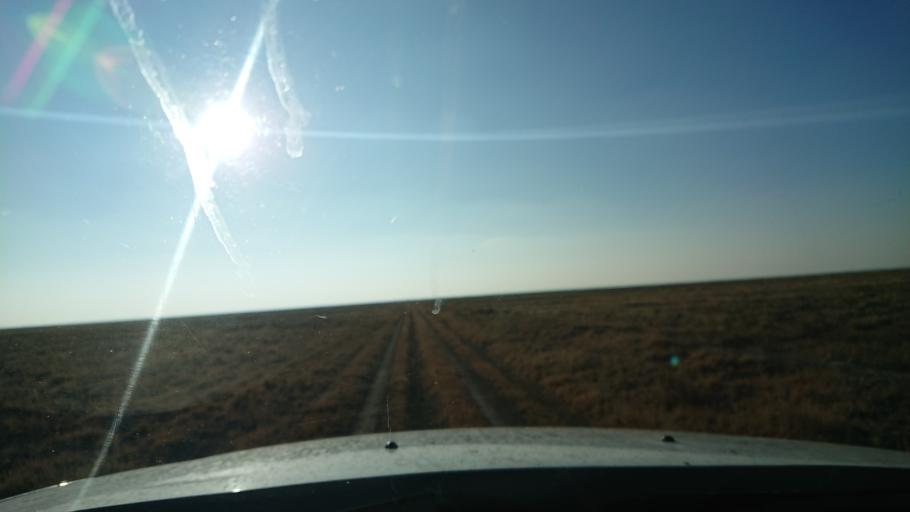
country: TR
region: Aksaray
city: Sultanhani
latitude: 38.3817
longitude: 33.5797
